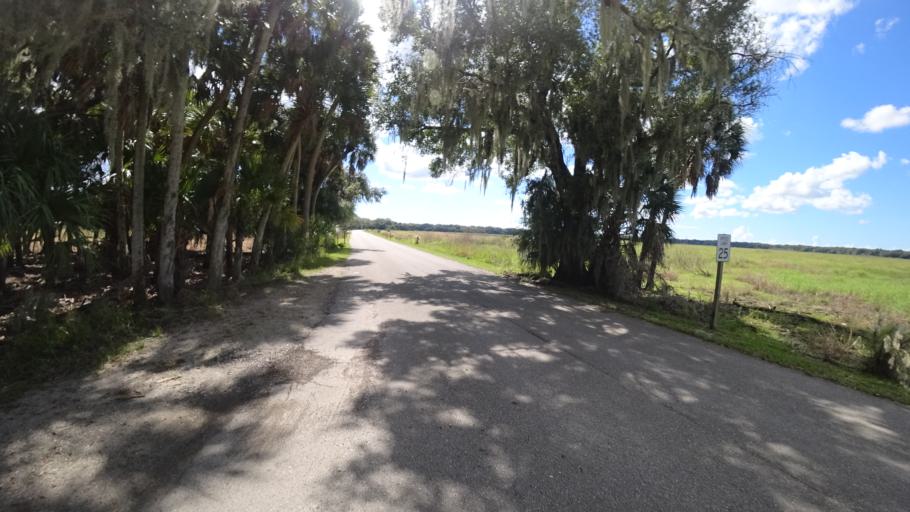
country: US
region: Florida
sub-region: Sarasota County
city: Lake Sarasota
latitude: 27.2595
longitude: -82.2876
